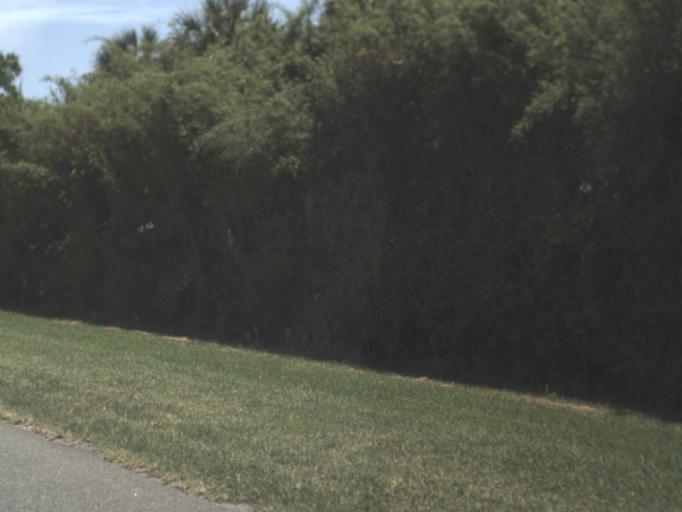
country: US
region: Florida
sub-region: Saint Johns County
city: Ponte Vedra Beach
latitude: 30.2380
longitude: -81.3864
